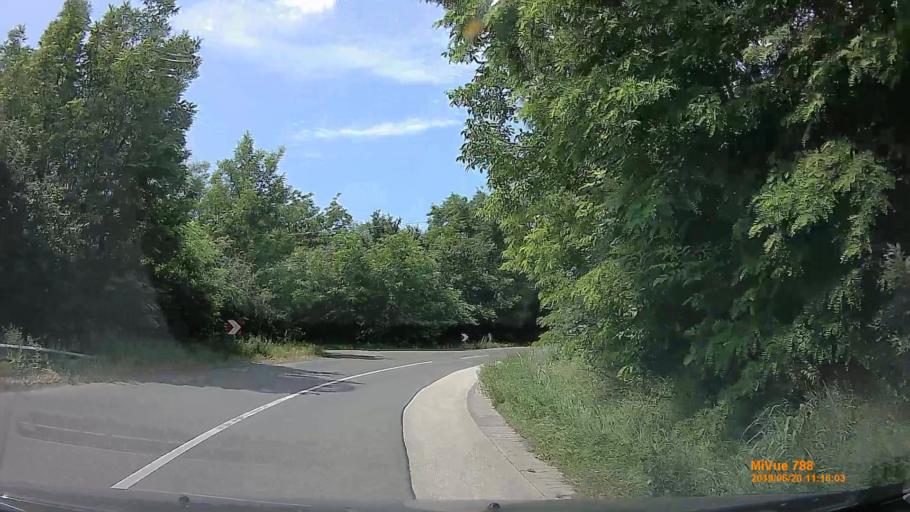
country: HU
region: Baranya
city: Pecsvarad
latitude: 46.1514
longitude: 18.4819
